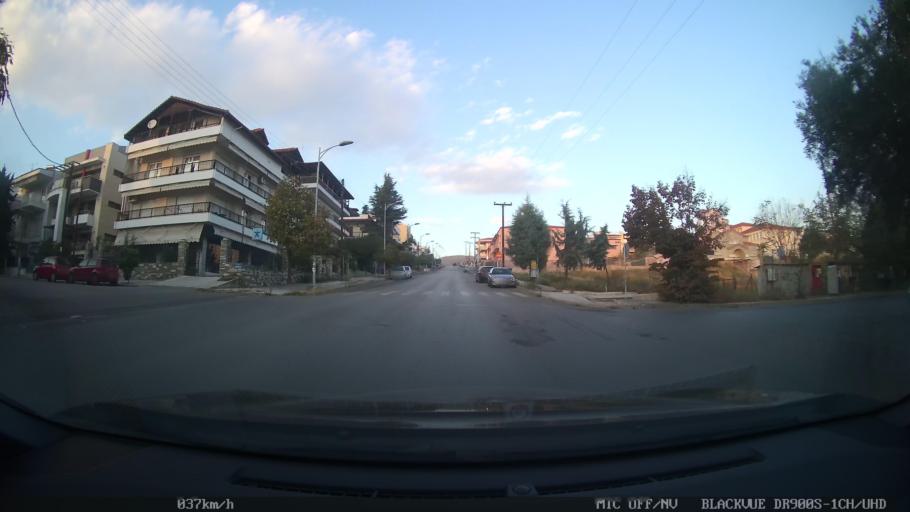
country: GR
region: Central Macedonia
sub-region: Nomos Thessalonikis
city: Pylaia
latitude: 40.6111
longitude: 22.9929
